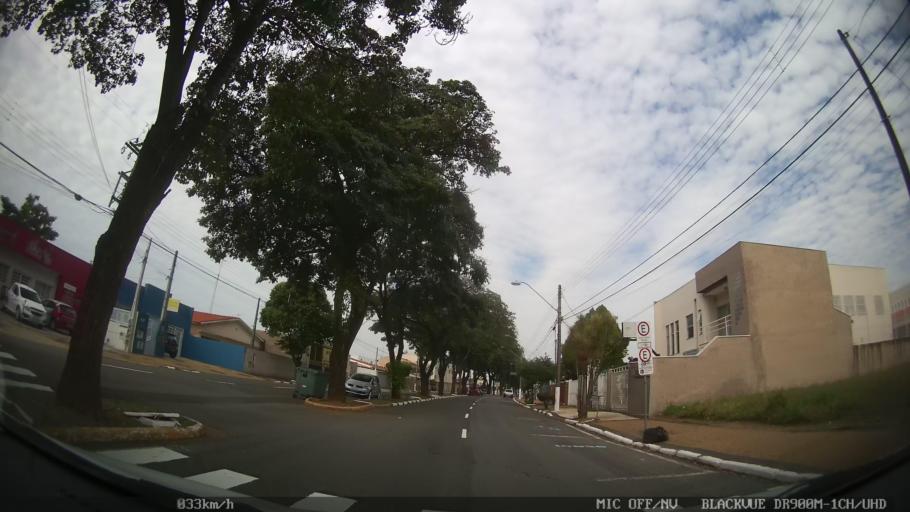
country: BR
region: Sao Paulo
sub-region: Paulinia
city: Paulinia
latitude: -22.7663
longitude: -47.1509
